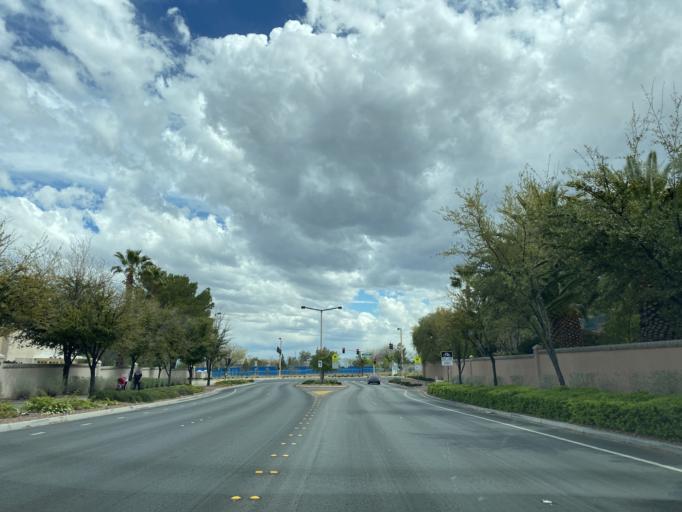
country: US
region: Nevada
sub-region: Clark County
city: Summerlin South
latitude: 36.1958
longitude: -115.2874
